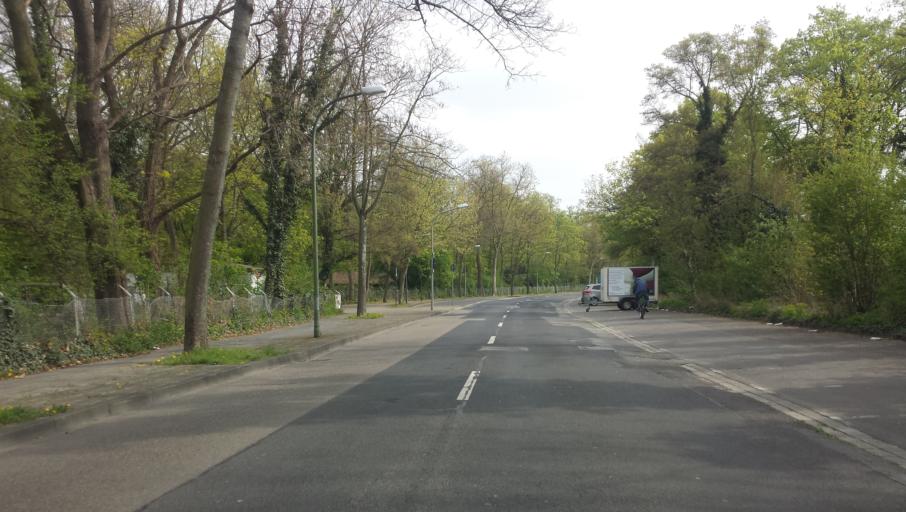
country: DE
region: Rheinland-Pfalz
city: Gartenstadt
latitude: 49.4903
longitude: 8.4112
